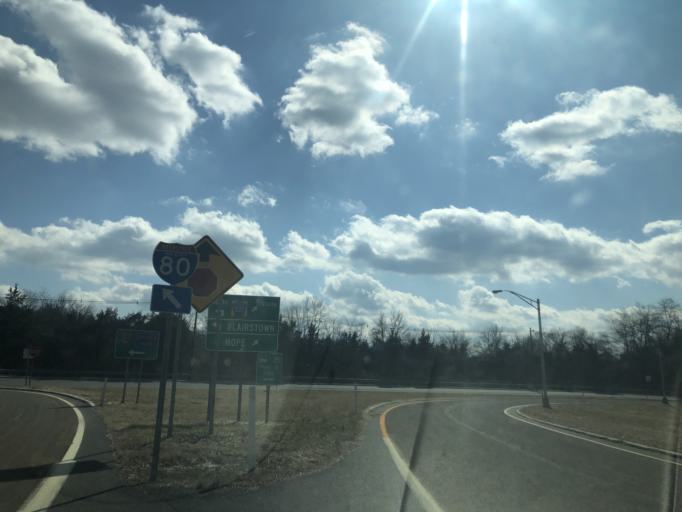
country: US
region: New Jersey
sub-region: Warren County
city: Oxford
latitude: 40.9227
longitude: -74.9614
